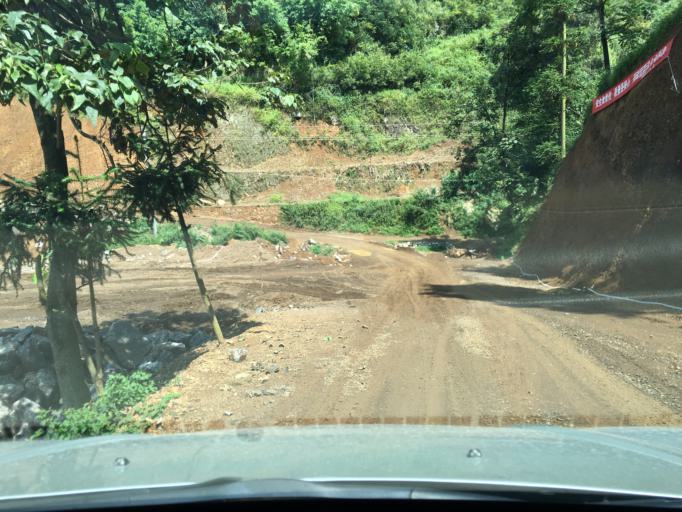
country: CN
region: Guizhou Sheng
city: Liupanshui
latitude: 25.9086
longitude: 105.1069
